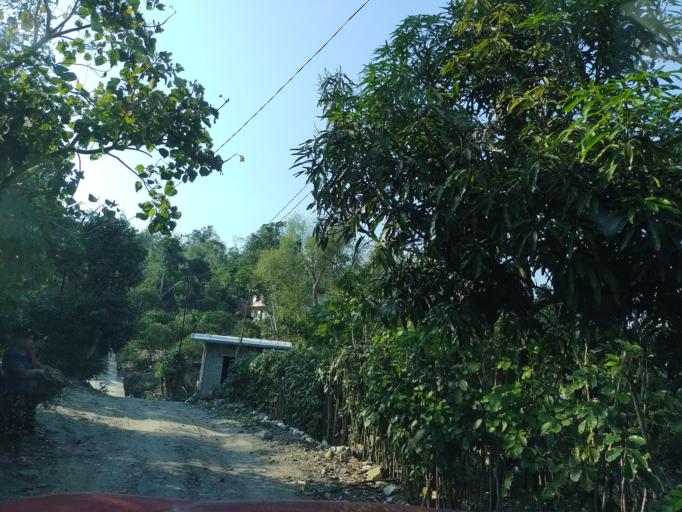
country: MX
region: Veracruz
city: Agua Dulce
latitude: 20.3705
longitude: -97.1848
